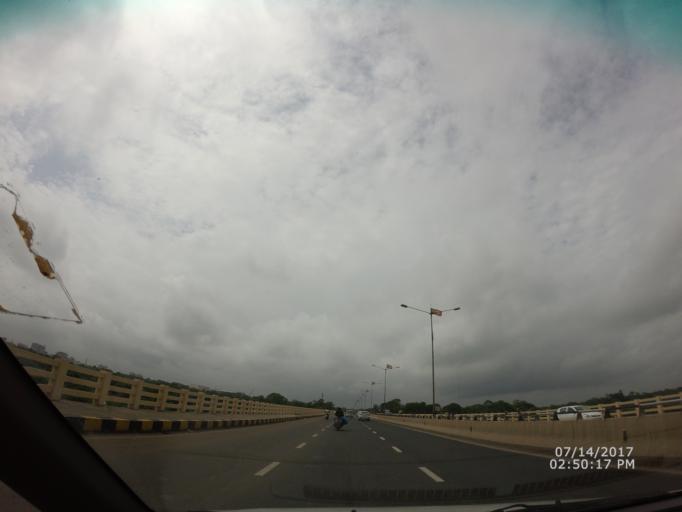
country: IN
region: Gujarat
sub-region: Ahmadabad
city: Naroda
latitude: 23.0907
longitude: 72.6299
